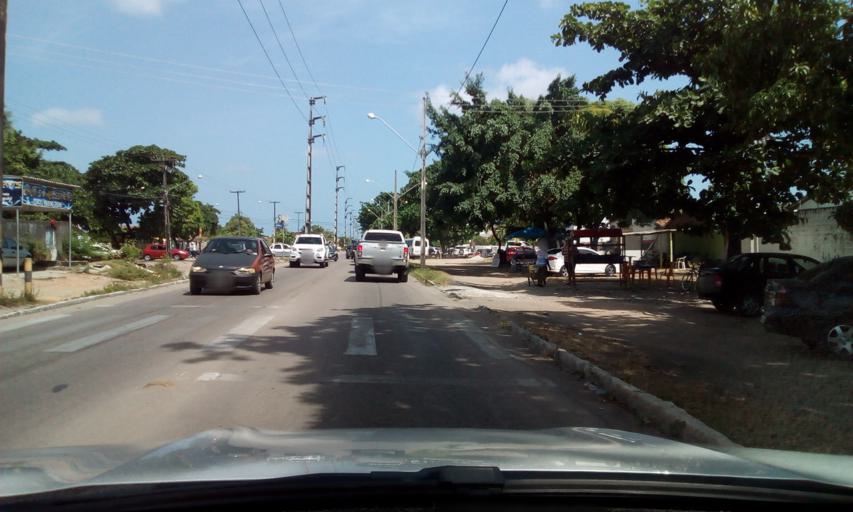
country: BR
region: Paraiba
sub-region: Joao Pessoa
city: Joao Pessoa
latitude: -7.1798
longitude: -34.8701
